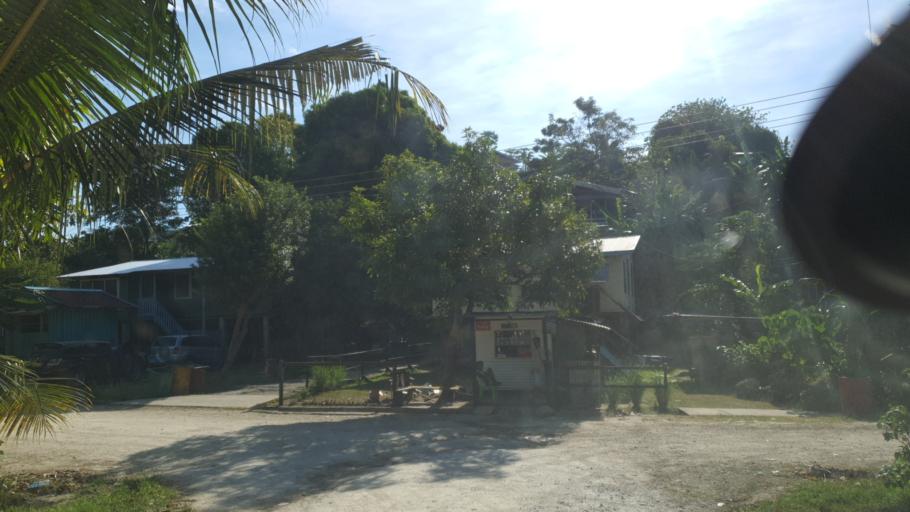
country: SB
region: Guadalcanal
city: Honiara
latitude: -9.4355
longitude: 160.0011
